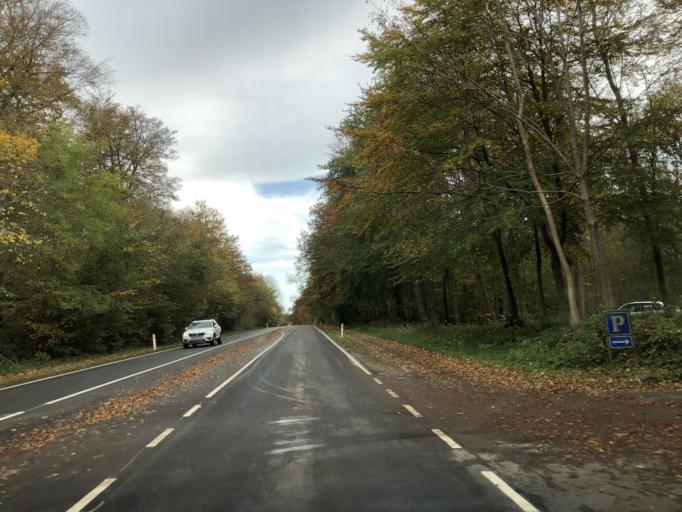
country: DK
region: Capital Region
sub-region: Hillerod Kommune
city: Hillerod
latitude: 55.9283
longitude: 12.3208
